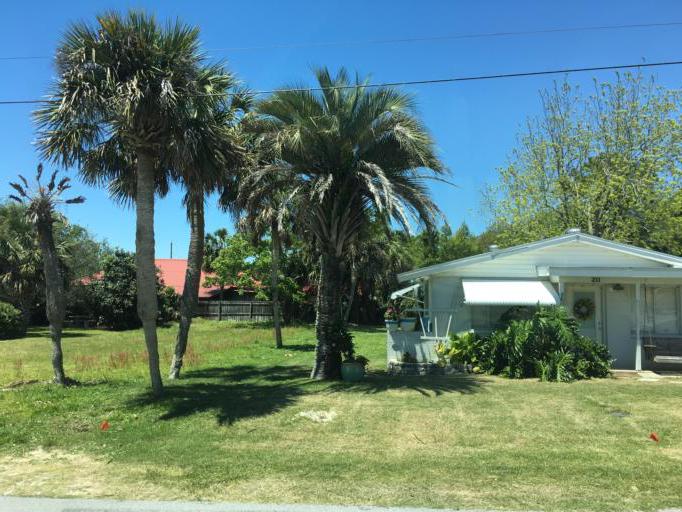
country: US
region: Florida
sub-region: Bay County
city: Laguna Beach
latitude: 30.2488
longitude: -85.9396
